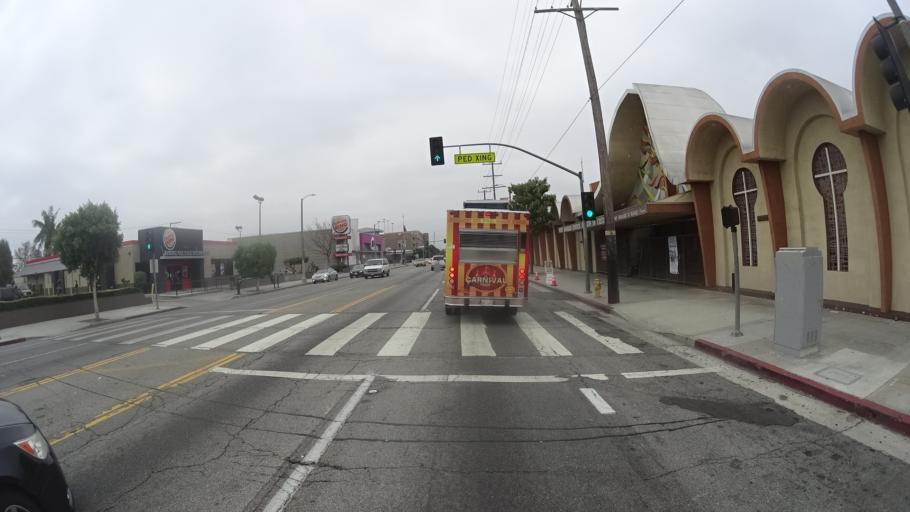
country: US
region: California
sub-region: Los Angeles County
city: View Park-Windsor Hills
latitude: 34.0275
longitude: -118.3352
